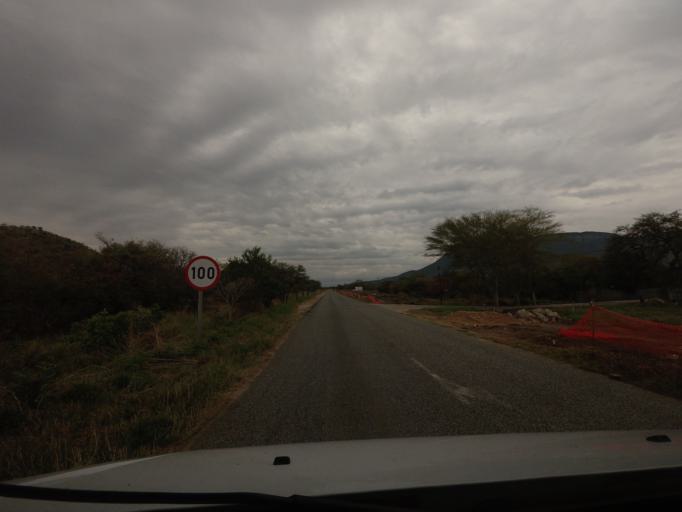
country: ZA
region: Limpopo
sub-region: Mopani District Municipality
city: Hoedspruit
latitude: -24.5011
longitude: 30.8965
